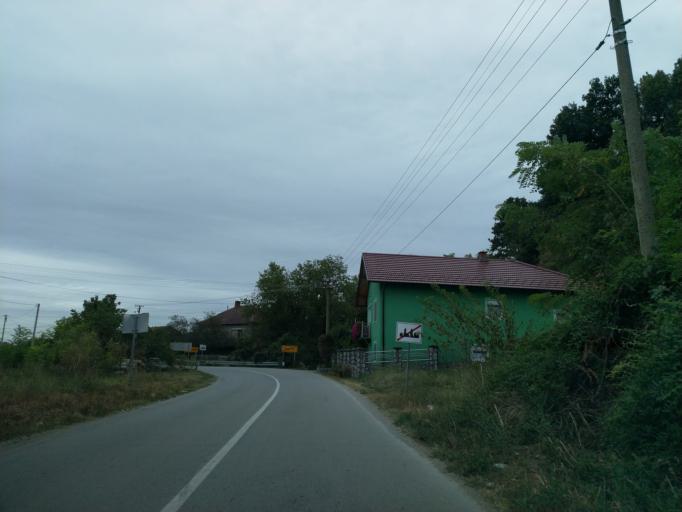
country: RS
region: Central Serbia
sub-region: Pomoravski Okrug
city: Cuprija
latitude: 43.8737
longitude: 21.3209
